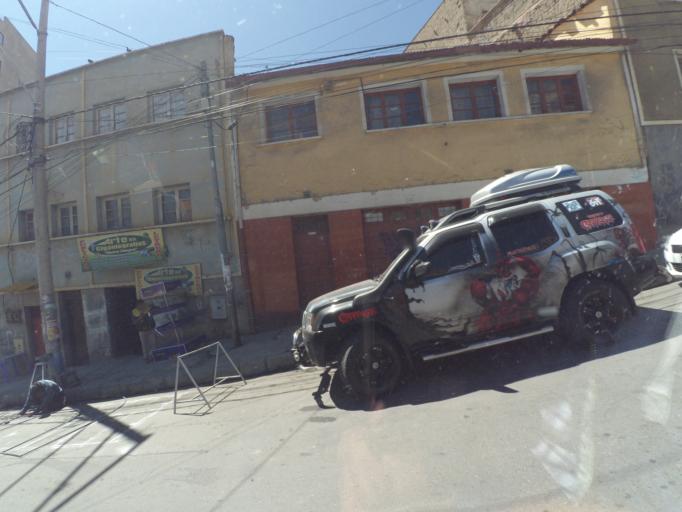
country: BO
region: La Paz
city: La Paz
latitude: -16.4935
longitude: -68.1481
